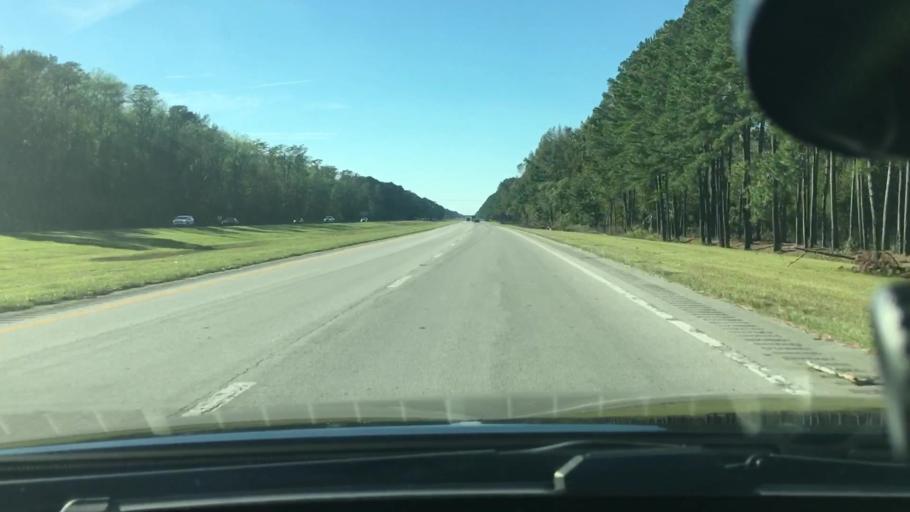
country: US
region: North Carolina
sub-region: Craven County
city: Trent Woods
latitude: 35.1204
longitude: -77.1116
